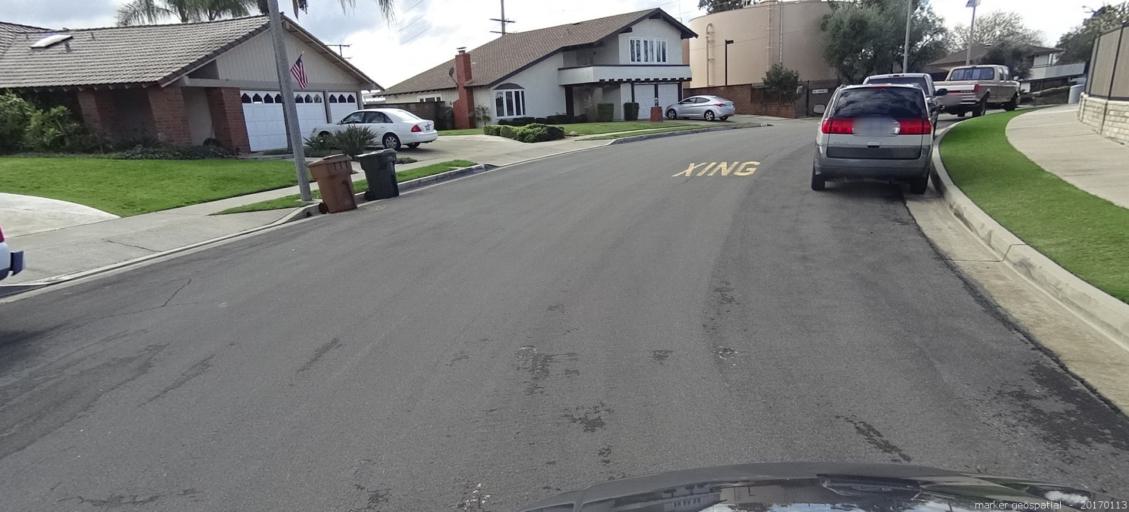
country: US
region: California
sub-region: Orange County
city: Yorba Linda
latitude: 33.8687
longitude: -117.7860
